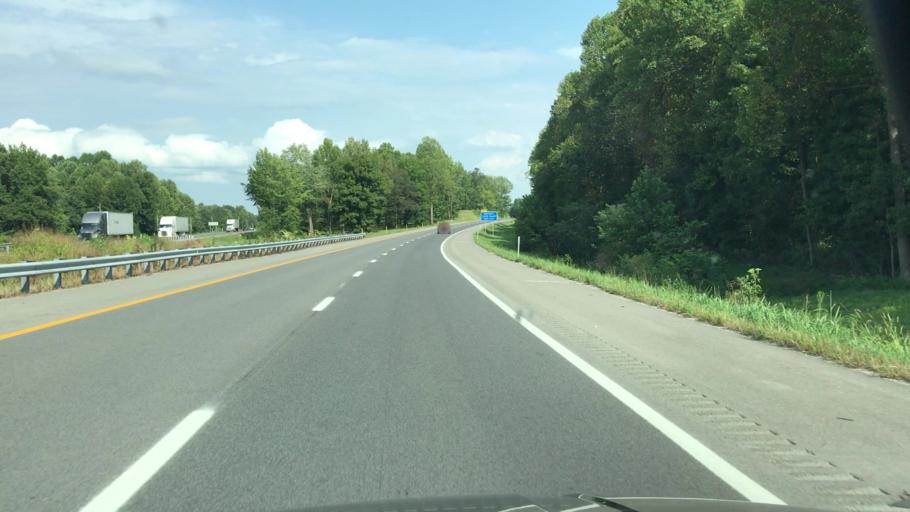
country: US
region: Kentucky
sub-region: Hopkins County
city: Nortonville
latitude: 37.2122
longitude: -87.4282
